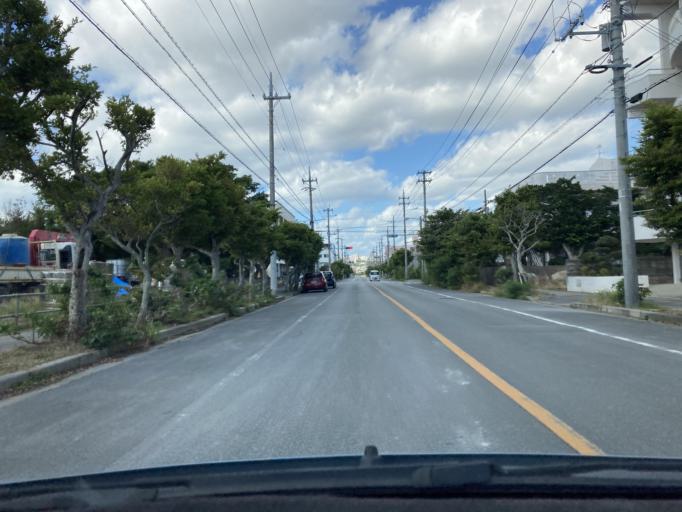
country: JP
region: Okinawa
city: Katsuren-haebaru
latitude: 26.3190
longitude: 127.8385
